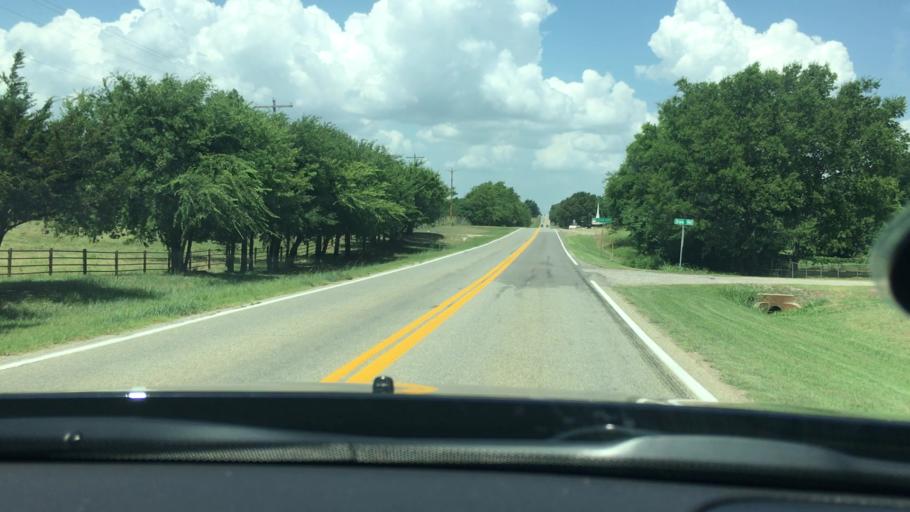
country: US
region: Oklahoma
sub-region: Marshall County
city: Kingston
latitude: 34.0854
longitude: -96.6086
